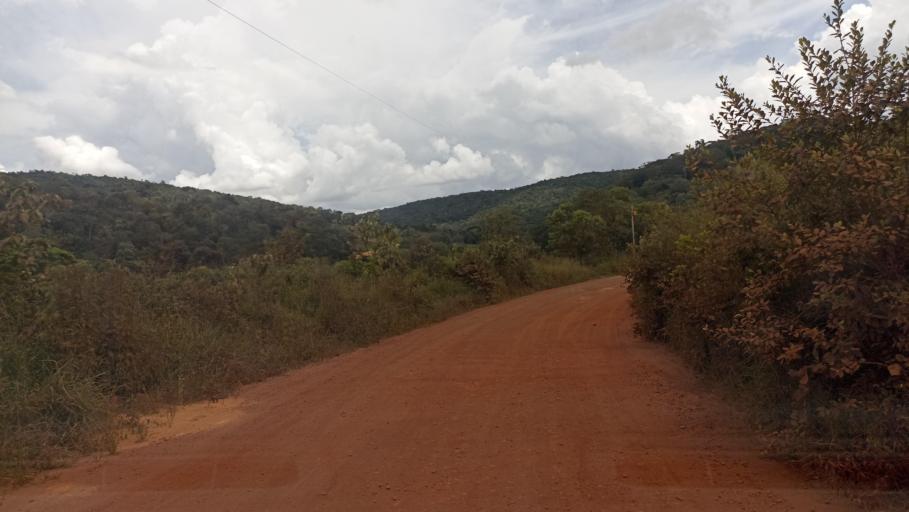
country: BR
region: Minas Gerais
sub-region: Itabirito
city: Itabirito
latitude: -20.3552
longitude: -43.7684
